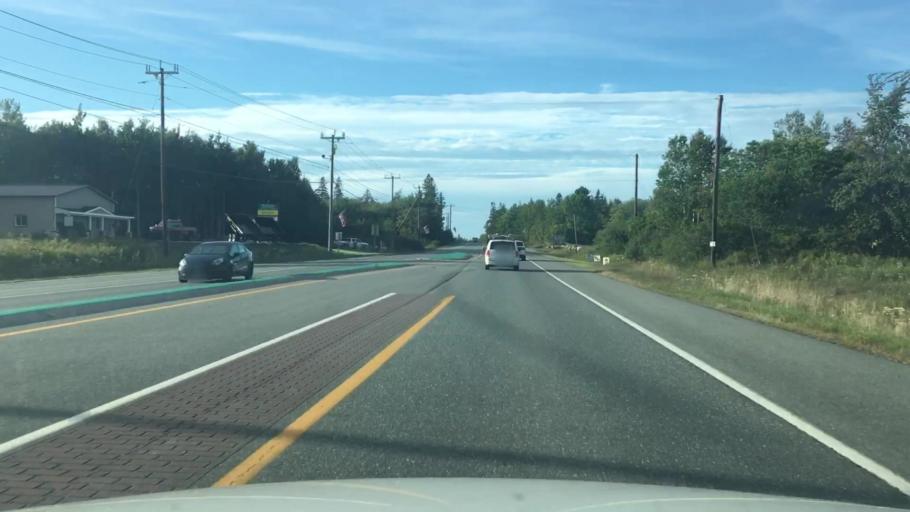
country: US
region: Maine
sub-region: Hancock County
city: Trenton
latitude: 44.4712
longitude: -68.3643
